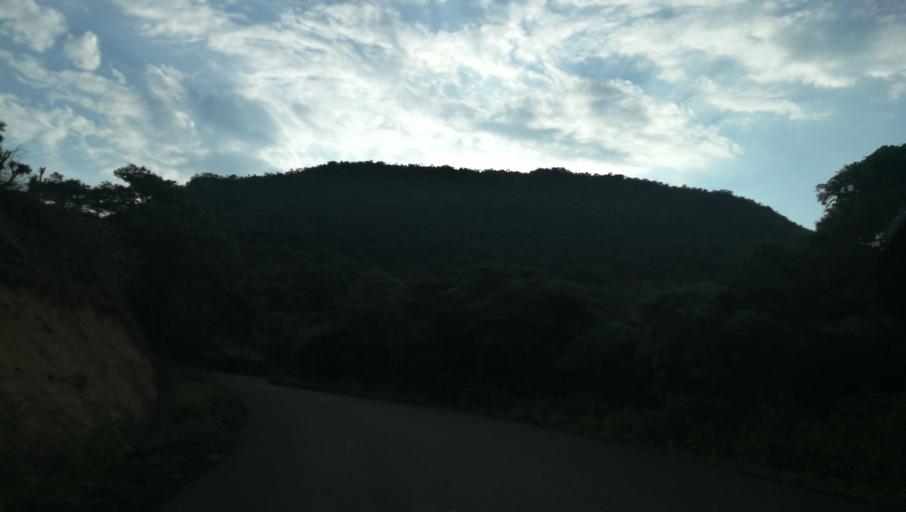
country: ET
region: Southern Nations, Nationalities, and People's Region
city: Areka
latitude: 6.8496
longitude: 37.2734
